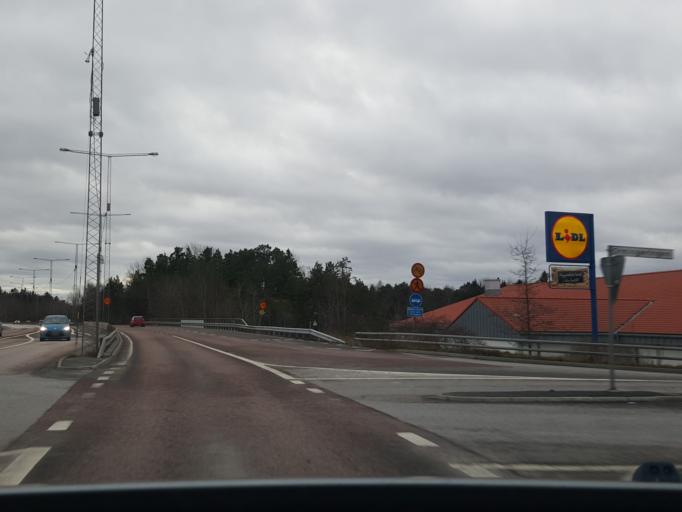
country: SE
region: Stockholm
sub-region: Nacka Kommun
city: Boo
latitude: 59.3236
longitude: 18.2581
